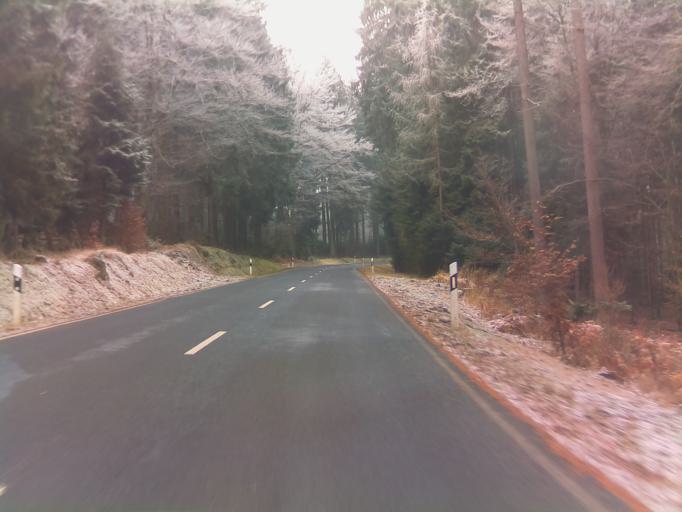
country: DE
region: Hesse
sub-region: Regierungsbezirk Darmstadt
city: Steinau an der Strasse
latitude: 50.2393
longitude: 9.4556
